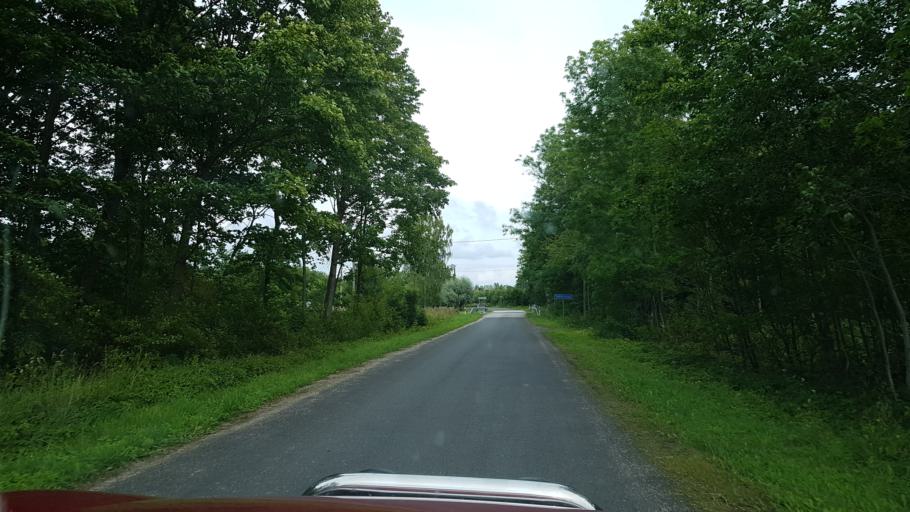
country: EE
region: Laeaene
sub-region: Ridala Parish
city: Uuemoisa
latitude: 58.9769
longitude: 23.7813
